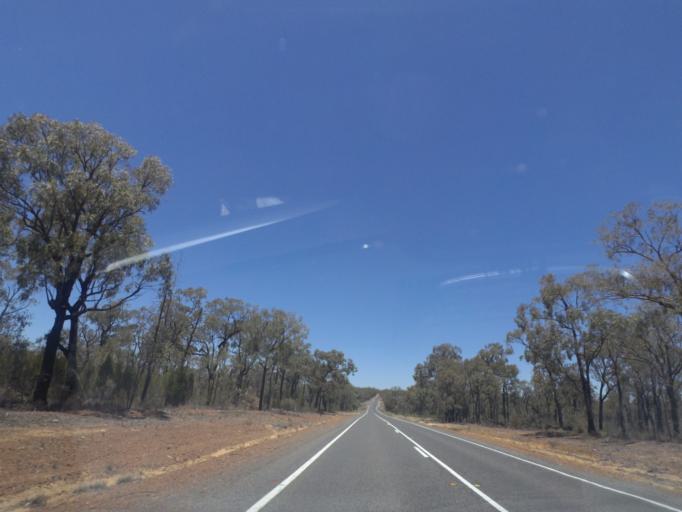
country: AU
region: New South Wales
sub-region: Narrabri
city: Narrabri
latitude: -30.7184
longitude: 149.5266
